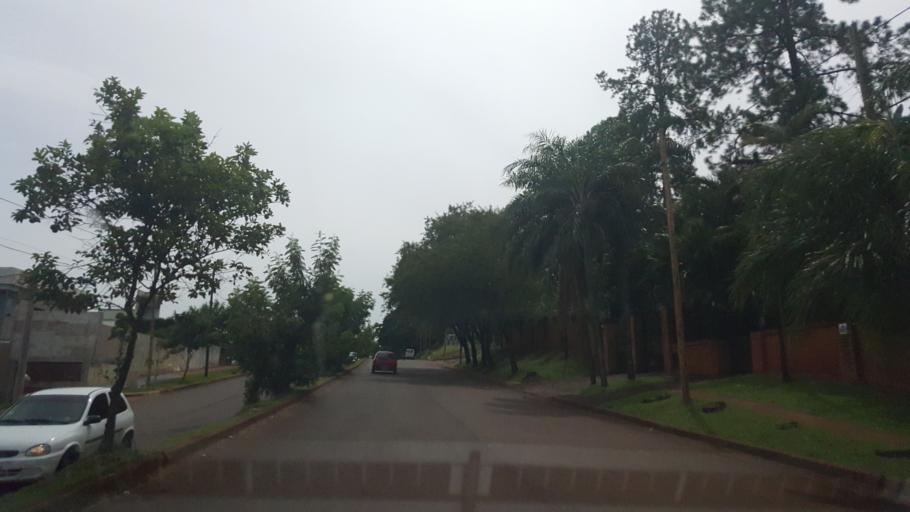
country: AR
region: Misiones
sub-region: Departamento de Capital
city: Posadas
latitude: -27.3990
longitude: -55.9438
